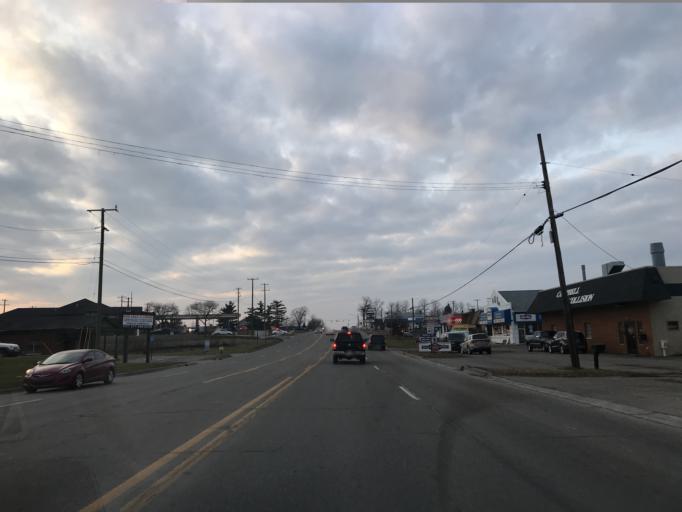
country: US
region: Michigan
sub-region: Livingston County
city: Brighton
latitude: 42.5212
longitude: -83.7597
